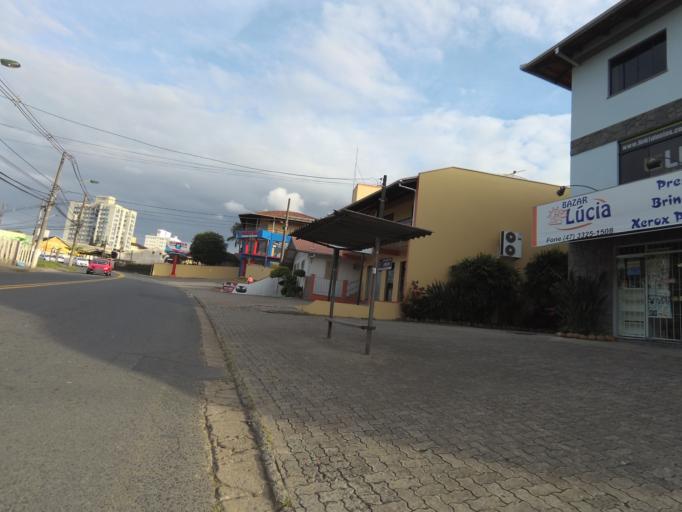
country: BR
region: Santa Catarina
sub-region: Blumenau
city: Blumenau
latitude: -26.9109
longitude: -49.1168
